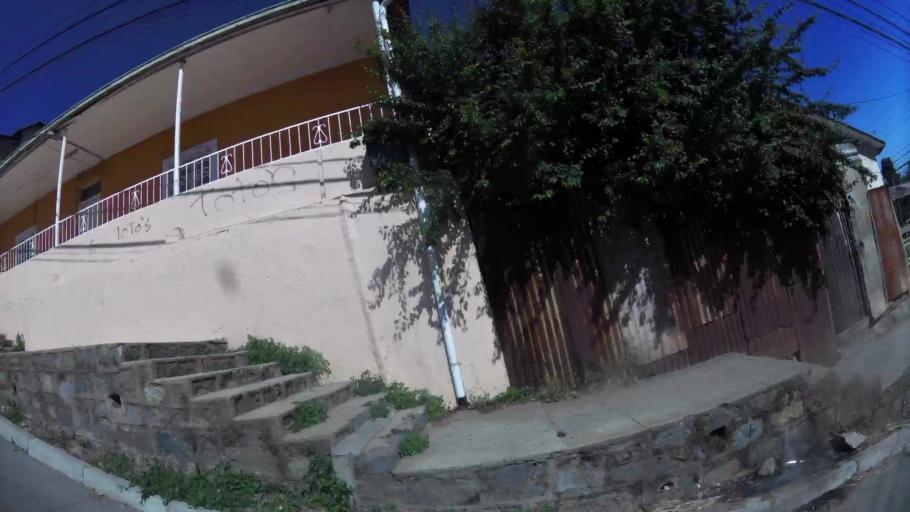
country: CL
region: Valparaiso
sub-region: Provincia de Valparaiso
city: Valparaiso
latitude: -33.0608
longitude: -71.5931
